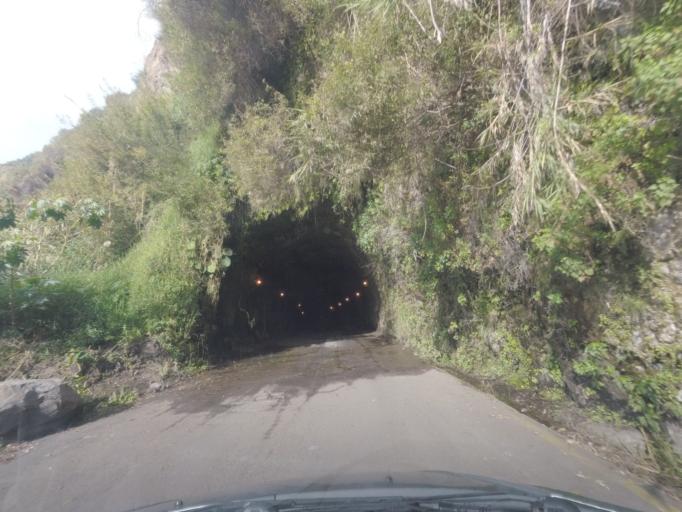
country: PT
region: Madeira
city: Ponta do Sol
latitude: 32.6908
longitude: -17.1199
